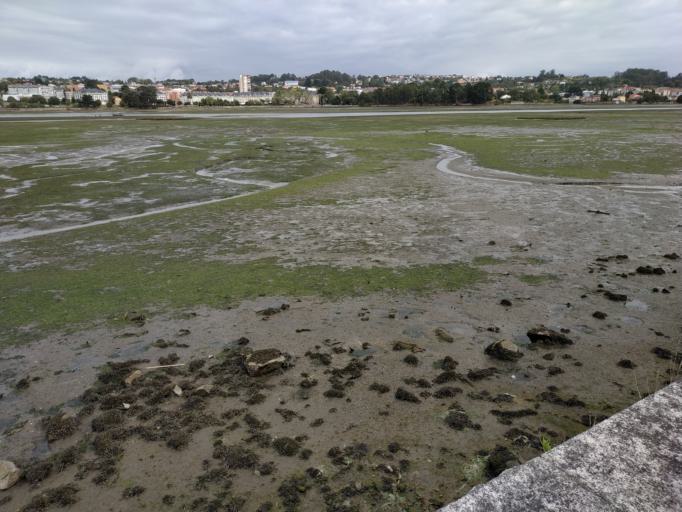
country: ES
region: Galicia
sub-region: Provincia da Coruna
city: Culleredo
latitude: 43.3246
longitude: -8.3790
